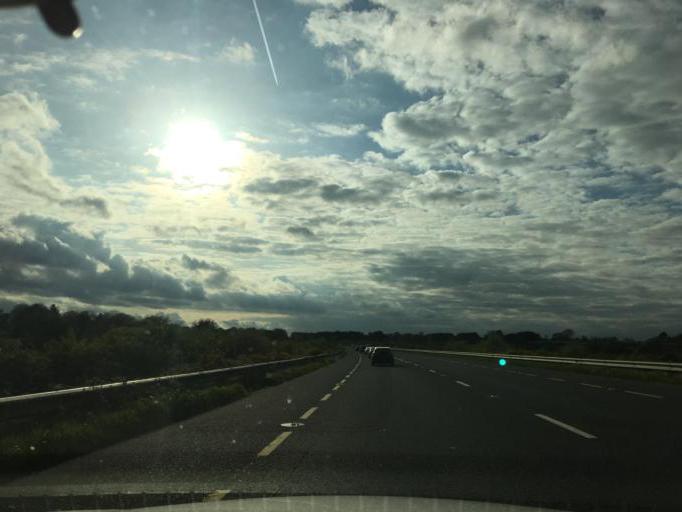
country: IE
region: Leinster
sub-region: Loch Garman
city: Enniscorthy
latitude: 52.3497
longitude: -6.6299
